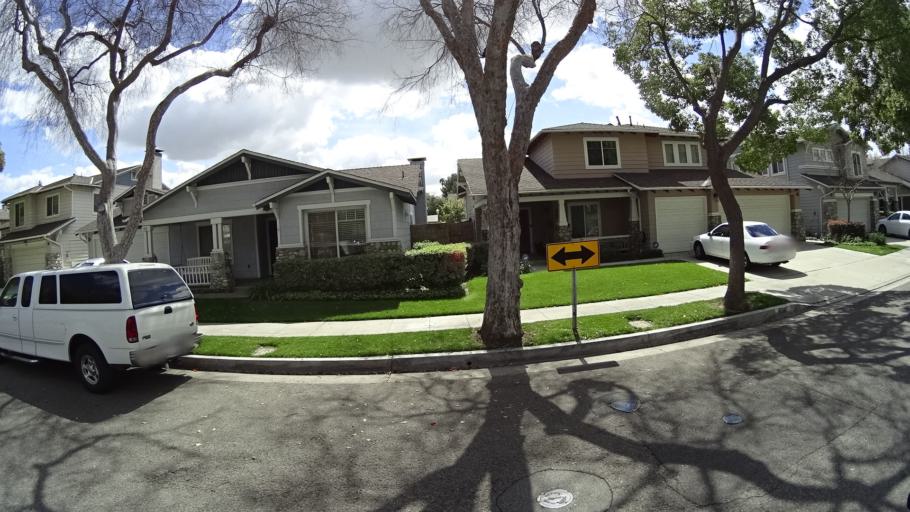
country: US
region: California
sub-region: Orange County
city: Anaheim
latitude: 33.8391
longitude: -117.9084
